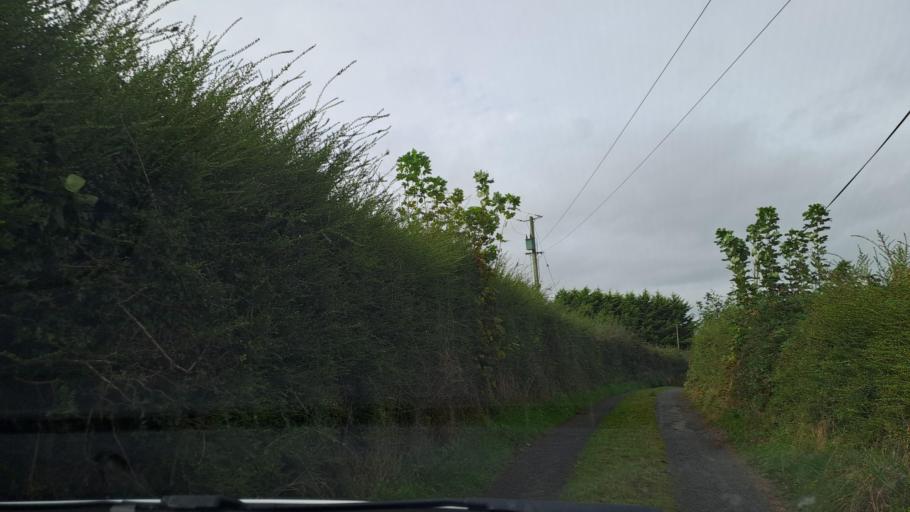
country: IE
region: Ulster
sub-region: An Cabhan
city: Bailieborough
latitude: 54.0037
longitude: -6.9466
